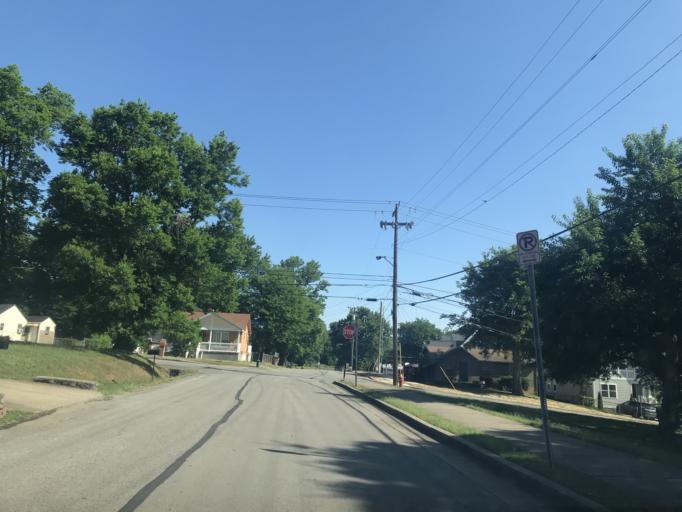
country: US
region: Tennessee
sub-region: Davidson County
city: Nashville
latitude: 36.1900
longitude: -86.8084
